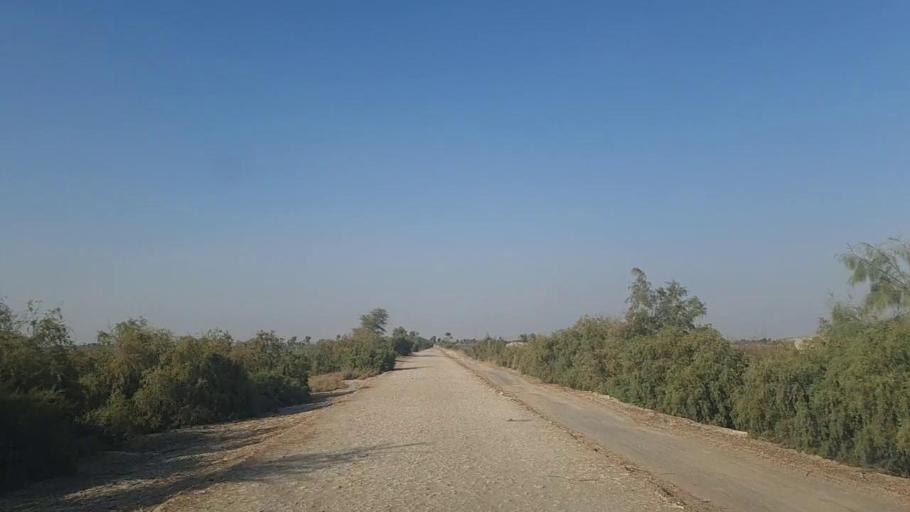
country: PK
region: Sindh
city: Jam Sahib
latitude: 26.3268
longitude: 68.7145
